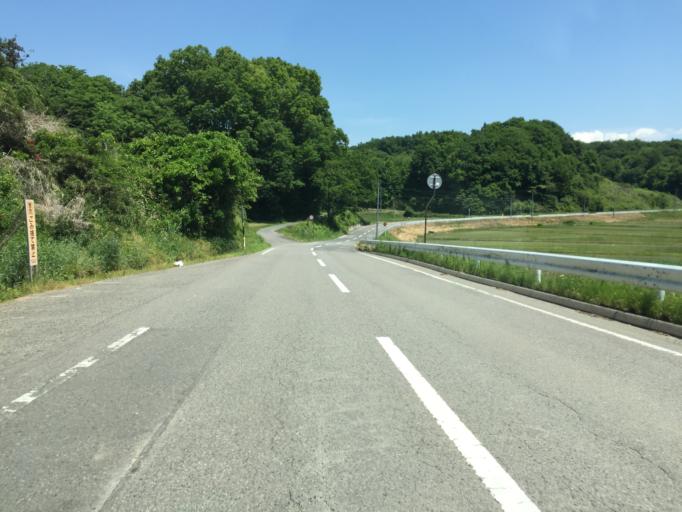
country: JP
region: Fukushima
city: Miharu
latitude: 37.4994
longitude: 140.4807
